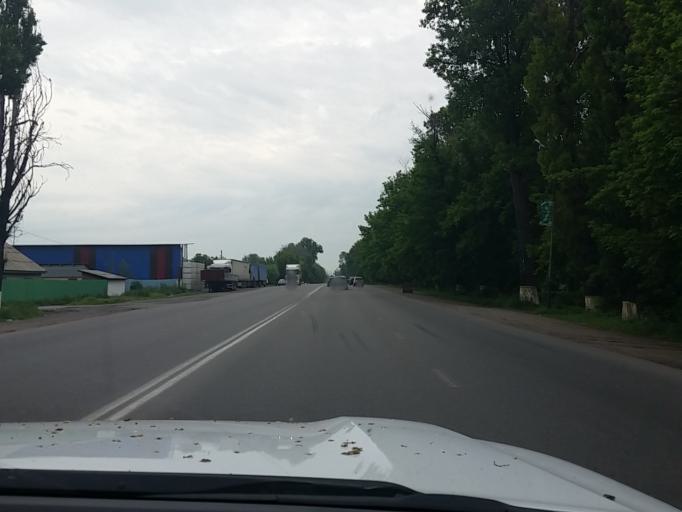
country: KZ
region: Almaty Oblysy
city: Energeticheskiy
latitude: 43.3421
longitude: 77.0483
